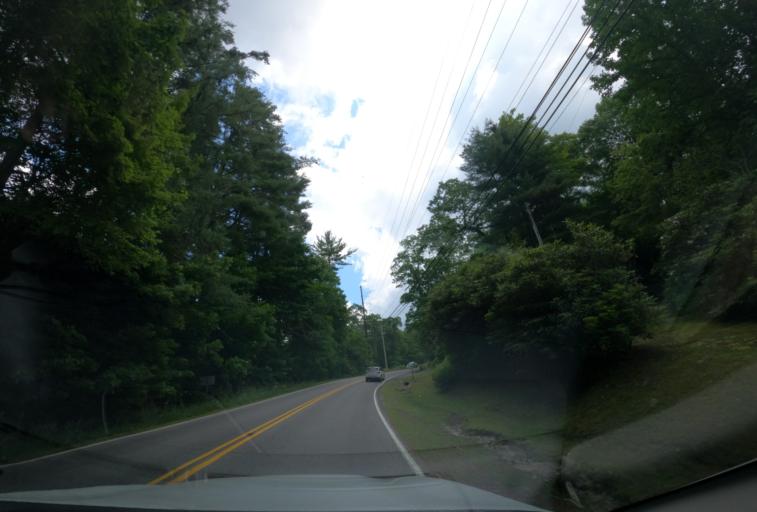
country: US
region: North Carolina
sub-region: Macon County
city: Franklin
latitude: 35.0844
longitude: -83.1844
